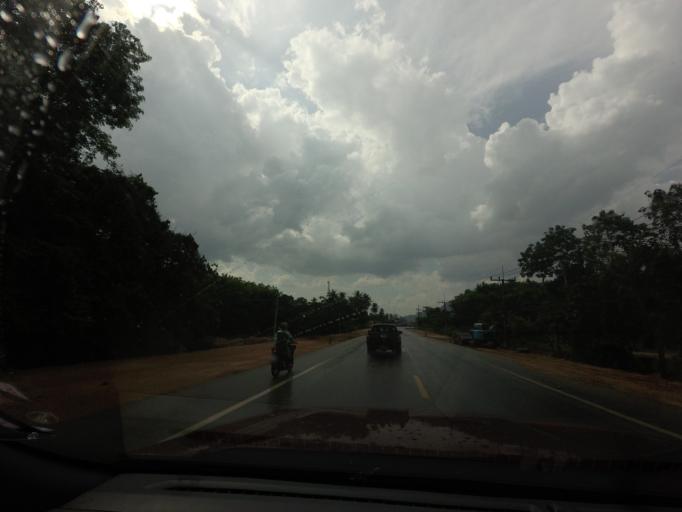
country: TH
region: Yala
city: Krong Pi Nang
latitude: 6.4087
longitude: 101.2802
